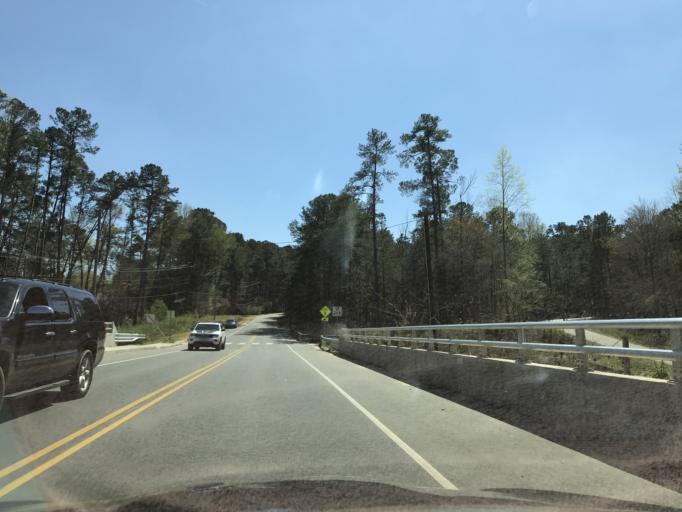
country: US
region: North Carolina
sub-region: Wake County
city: West Raleigh
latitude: 35.7623
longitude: -78.7037
